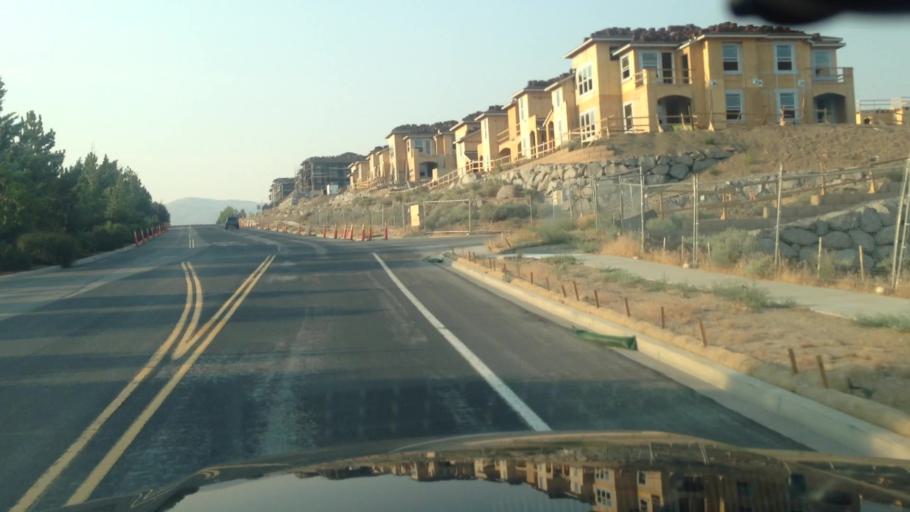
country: US
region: Nevada
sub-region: Washoe County
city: Mogul
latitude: 39.5163
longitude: -119.9004
